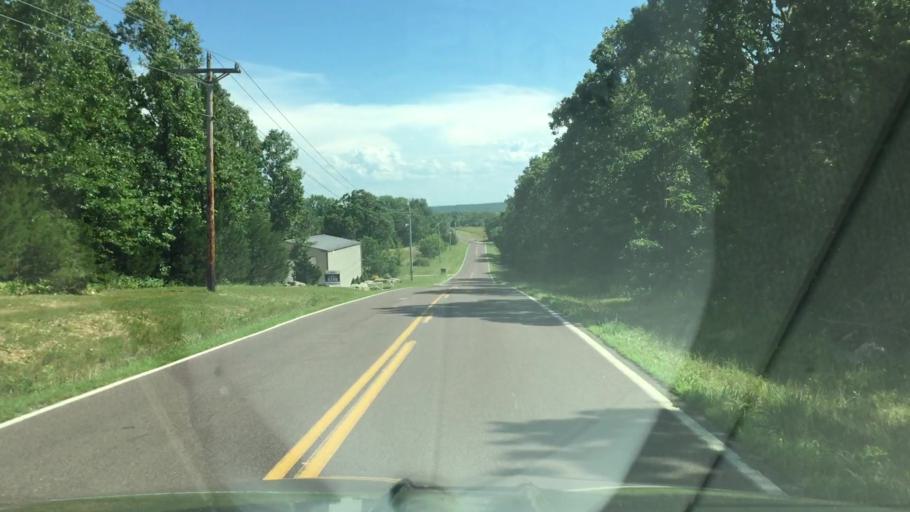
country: US
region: Missouri
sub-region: Miller County
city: Tuscumbia
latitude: 38.1126
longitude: -92.4723
